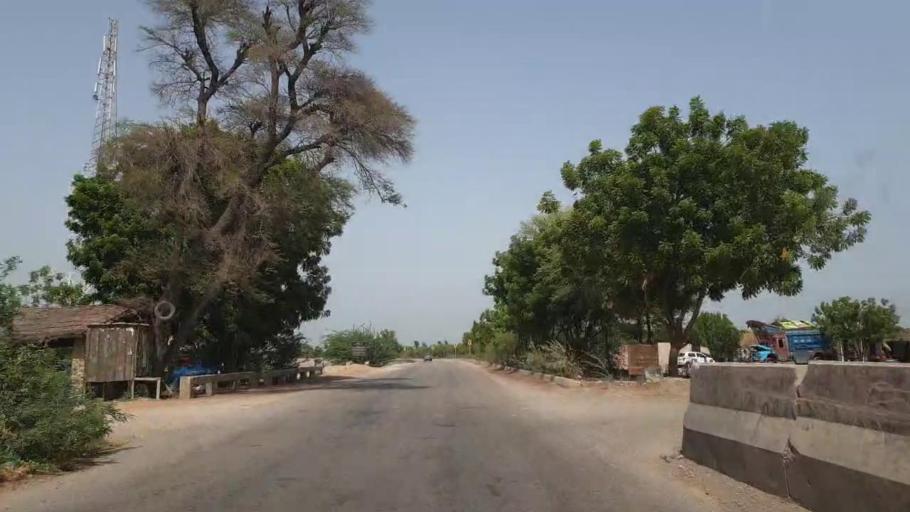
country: PK
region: Sindh
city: Sakrand
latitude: 26.1975
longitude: 68.3063
